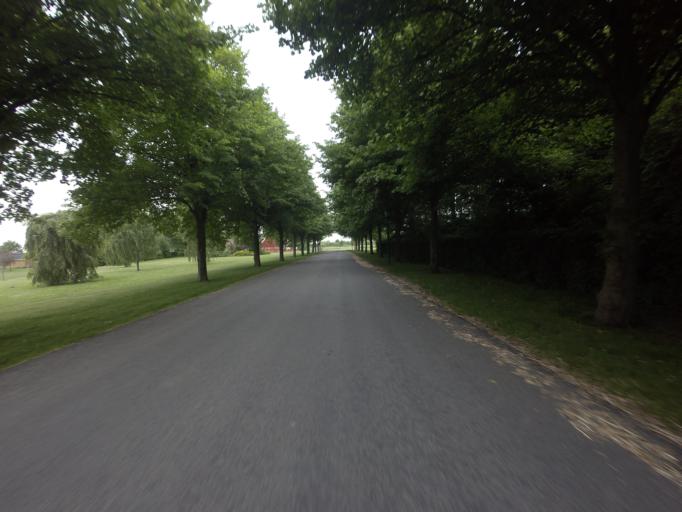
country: SE
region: Skane
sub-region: Angelholms Kommun
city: Strovelstorp
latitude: 56.1375
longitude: 12.7822
